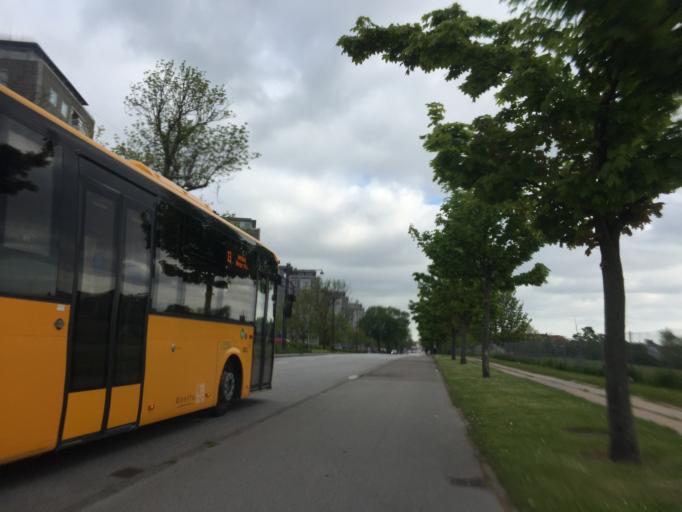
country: DK
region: Capital Region
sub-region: Kobenhavn
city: Vanlose
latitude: 55.7024
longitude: 12.5124
